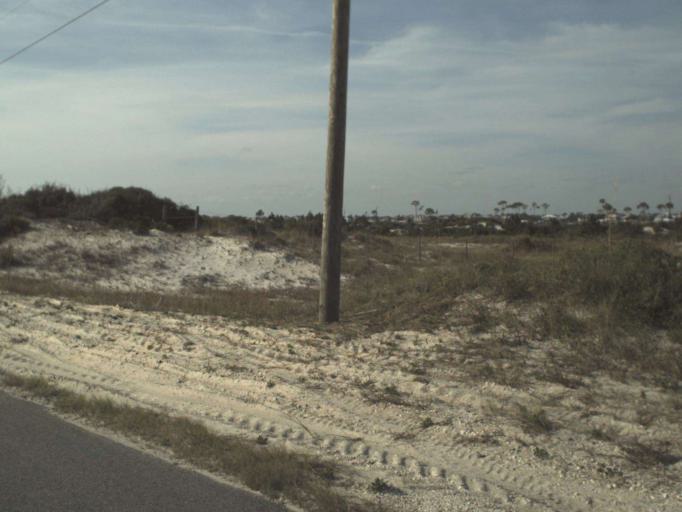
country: US
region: Alabama
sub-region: Baldwin County
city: Orange Beach
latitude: 30.2940
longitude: -87.4527
